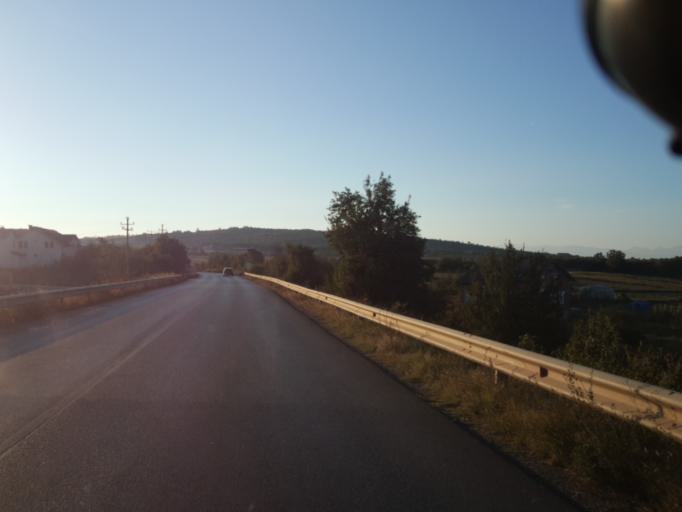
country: XK
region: Pec
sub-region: Komuna e Klines
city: Klina
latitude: 42.5914
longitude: 20.6639
